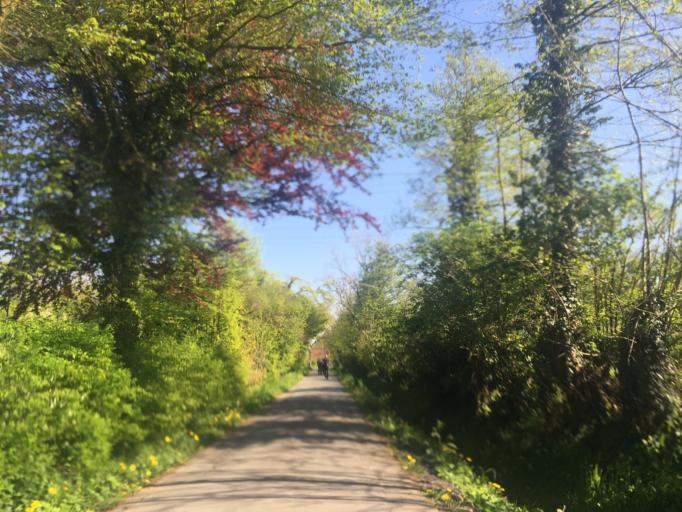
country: DE
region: North Rhine-Westphalia
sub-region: Regierungsbezirk Munster
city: Muenster
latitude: 51.9833
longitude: 7.5833
